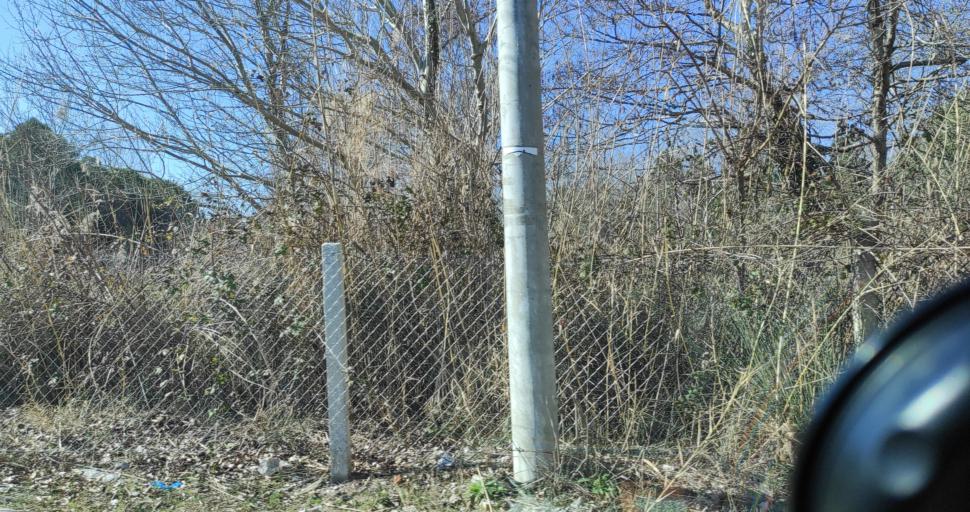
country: AL
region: Shkoder
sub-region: Rrethi i Shkodres
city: Velipoje
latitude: 41.8635
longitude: 19.4065
